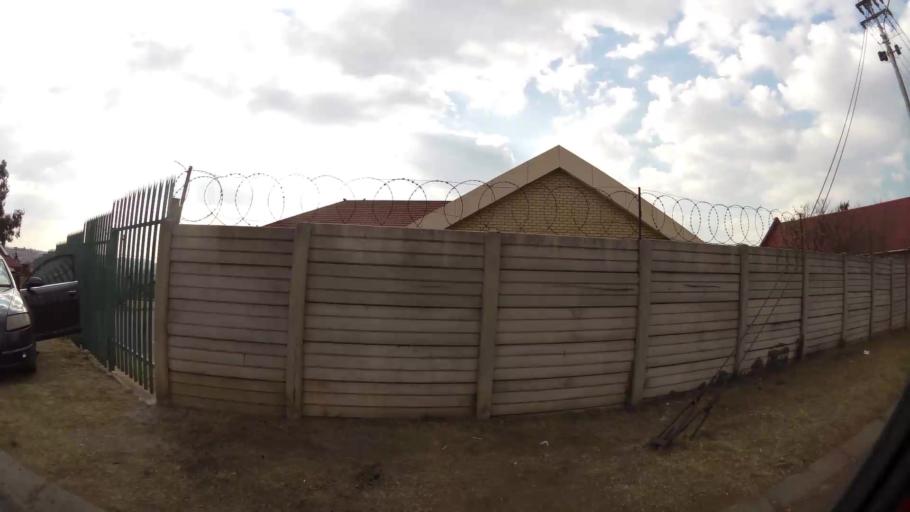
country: ZA
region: Gauteng
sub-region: City of Johannesburg Metropolitan Municipality
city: Soweto
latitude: -26.2258
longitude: 27.9330
